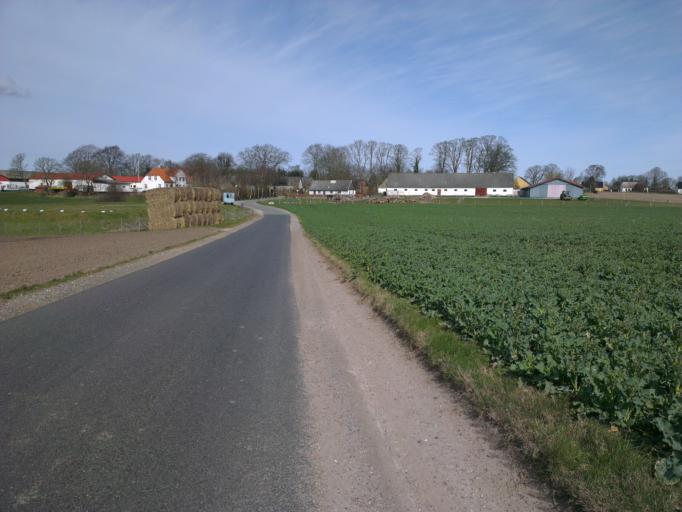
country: DK
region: Capital Region
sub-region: Frederikssund Kommune
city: Frederikssund
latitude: 55.8324
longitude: 12.1191
